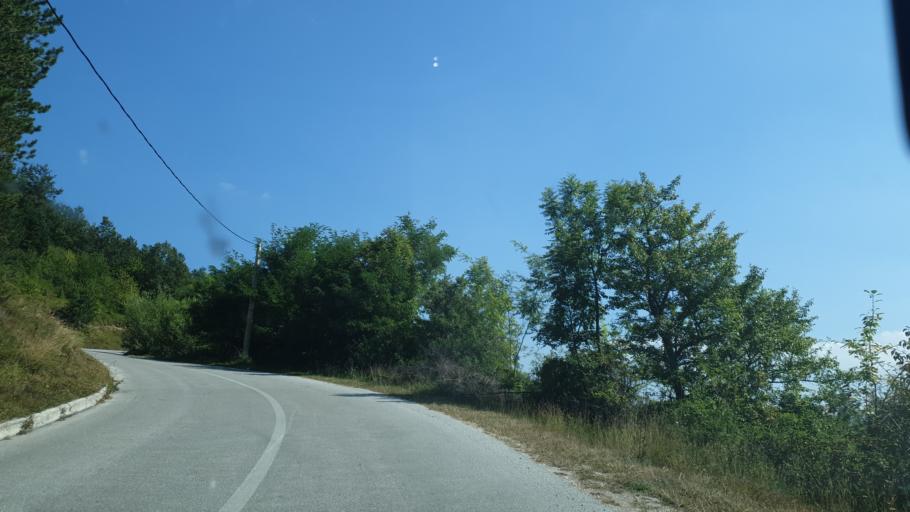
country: RS
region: Central Serbia
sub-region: Zlatiborski Okrug
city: Cajetina
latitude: 43.6760
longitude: 19.8323
